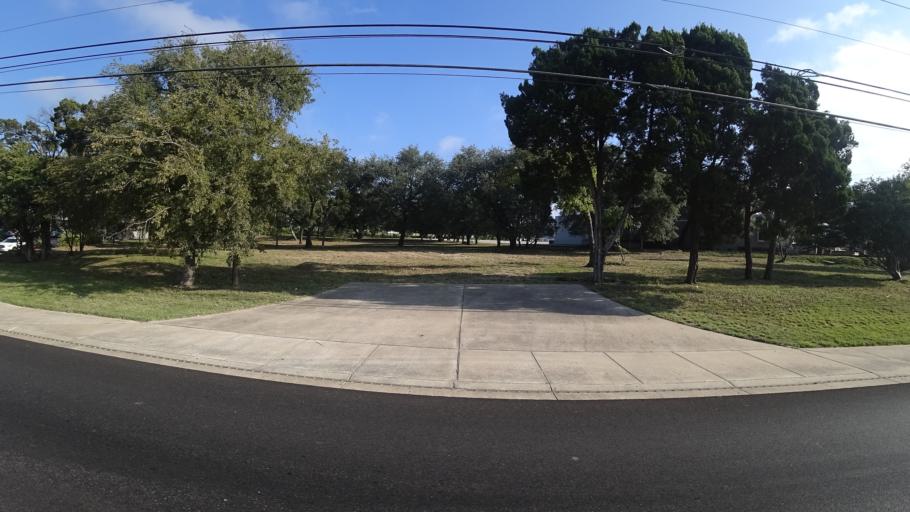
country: US
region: Texas
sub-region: Travis County
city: Austin
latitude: 30.3319
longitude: -97.6839
